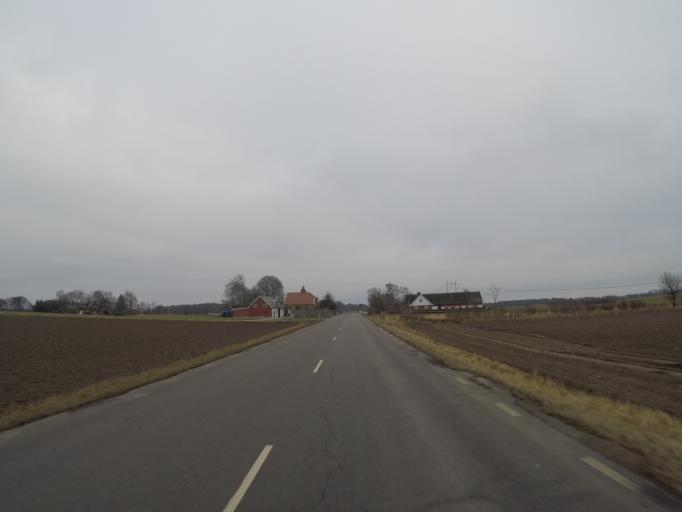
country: SE
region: Skane
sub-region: Hoors Kommun
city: Loberod
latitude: 55.7696
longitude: 13.4573
